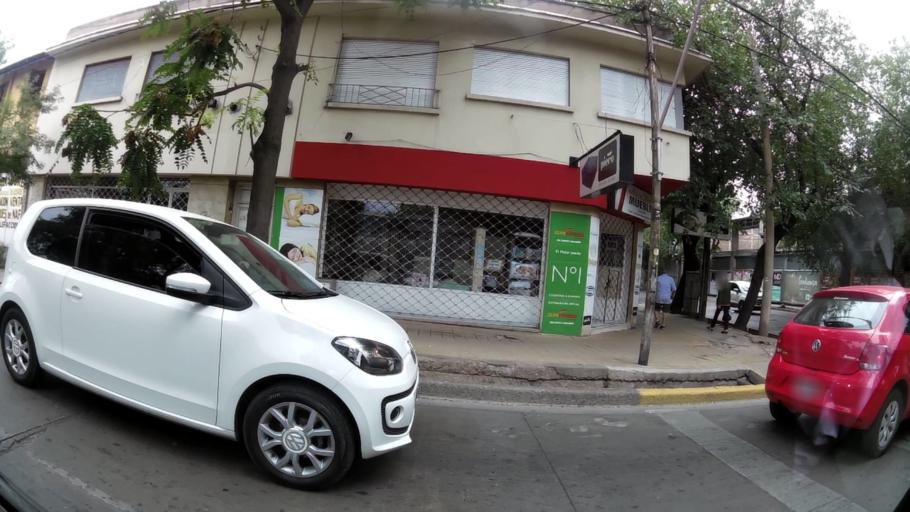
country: AR
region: Mendoza
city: Mendoza
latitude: -32.8821
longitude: -68.8387
